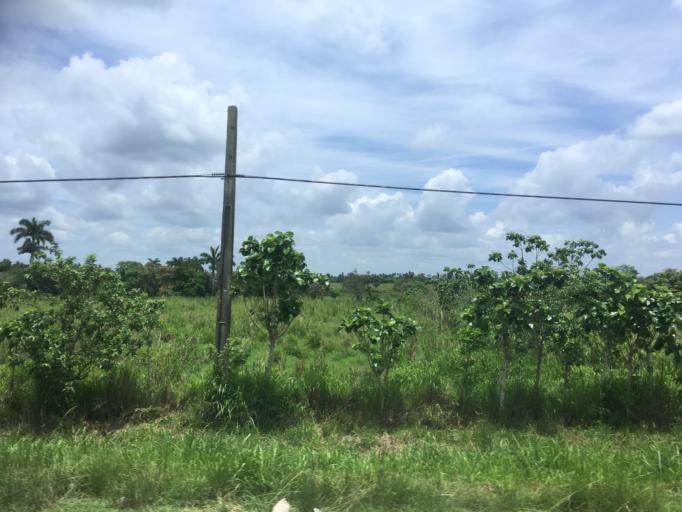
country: CU
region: Villa Clara
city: Esperanza
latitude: 22.4281
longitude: -80.0525
